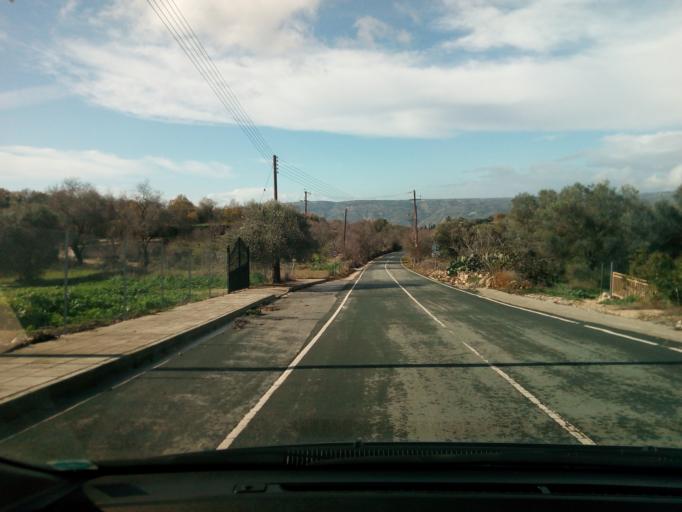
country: CY
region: Pafos
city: Tala
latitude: 34.9243
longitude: 32.5230
